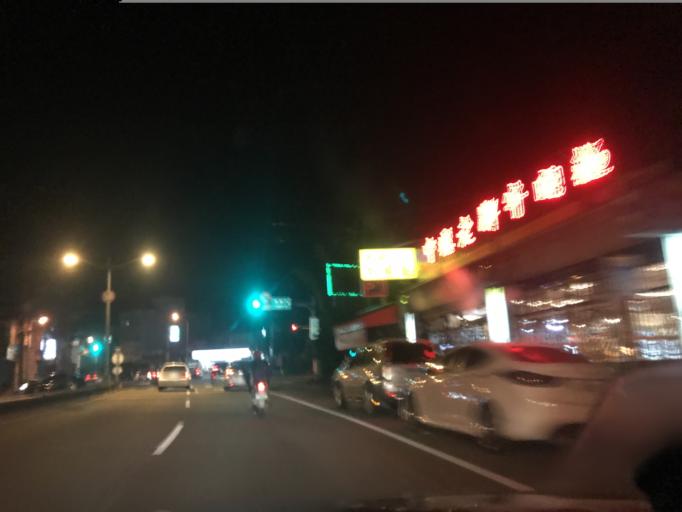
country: TW
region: Taiwan
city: Daxi
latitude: 24.8543
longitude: 121.2204
